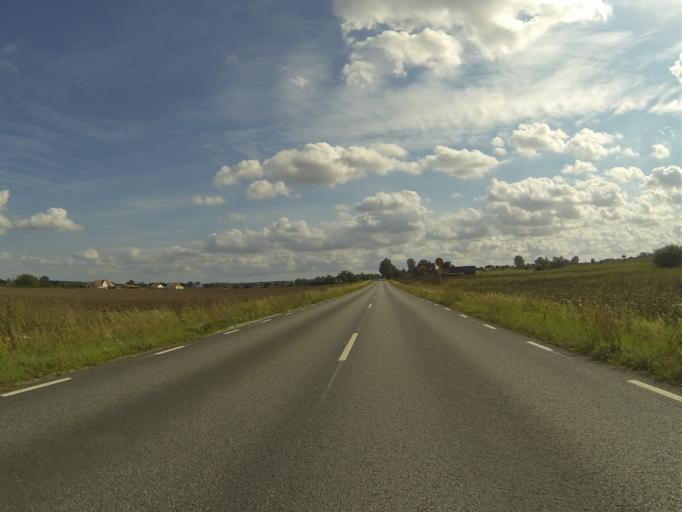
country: SE
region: Skane
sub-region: Eslovs Kommun
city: Eslov
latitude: 55.7449
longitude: 13.3269
